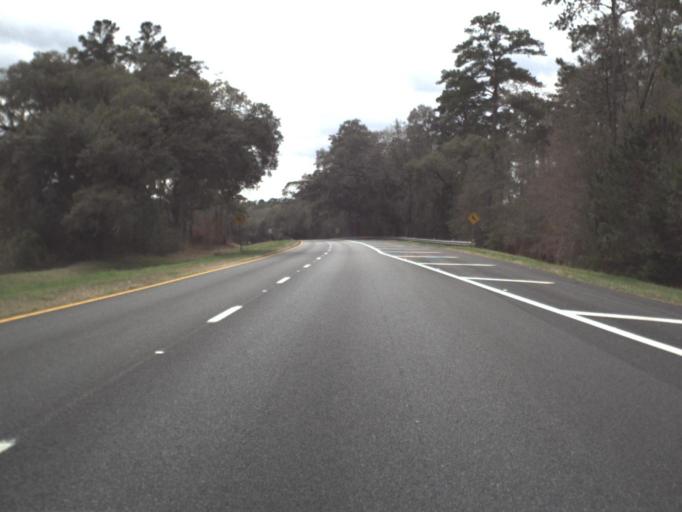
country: US
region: Georgia
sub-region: Grady County
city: Cairo
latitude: 30.6656
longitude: -84.1660
